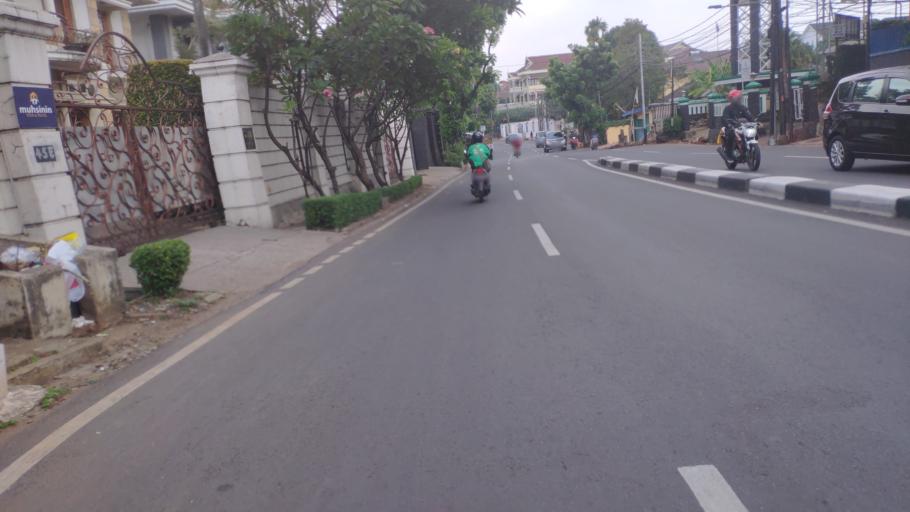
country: ID
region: Jakarta Raya
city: Jakarta
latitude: -6.2768
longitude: 106.8248
